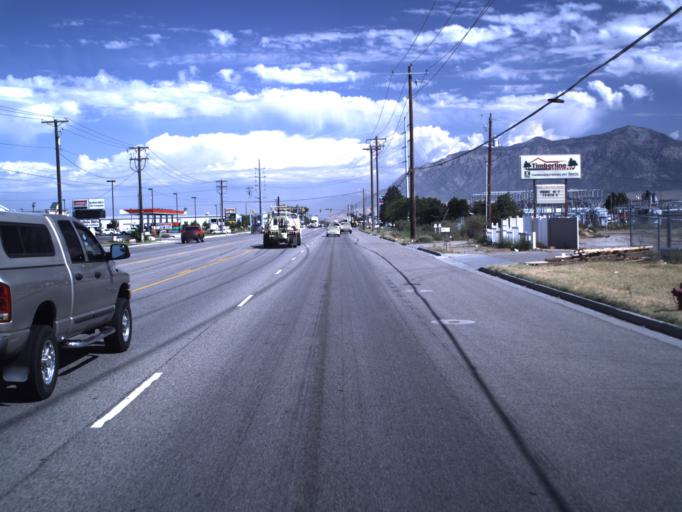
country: US
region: Utah
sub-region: Weber County
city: West Haven
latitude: 41.2168
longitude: -112.0256
